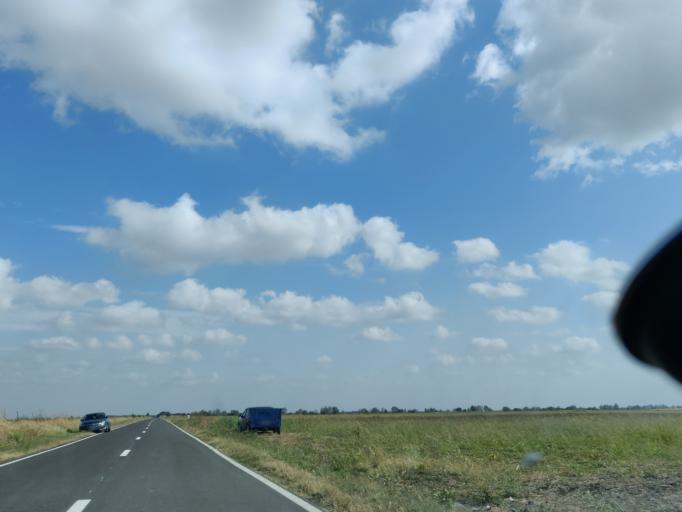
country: RO
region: Vrancea
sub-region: Comuna Maicanesti
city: Ramniceni
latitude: 45.4661
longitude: 27.4207
